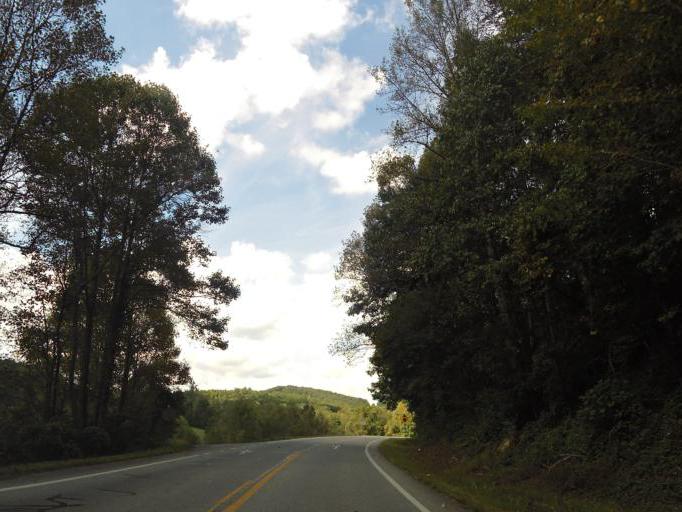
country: US
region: Georgia
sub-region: Pickens County
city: Jasper
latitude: 34.5362
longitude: -84.2617
